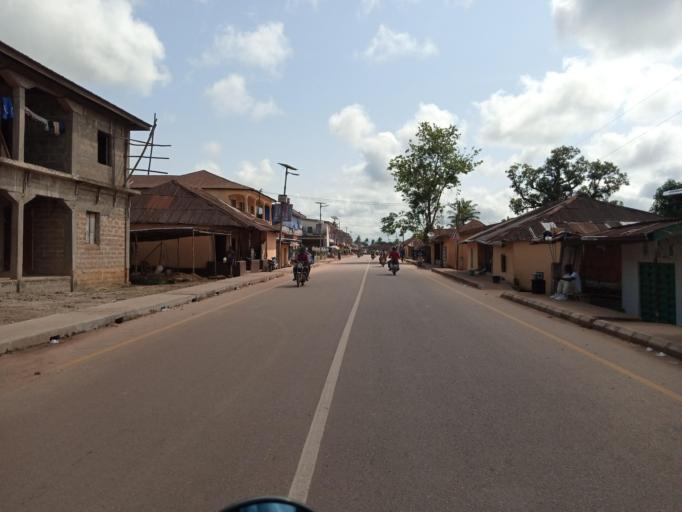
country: SL
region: Southern Province
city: Bo
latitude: 7.9685
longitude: -11.7392
